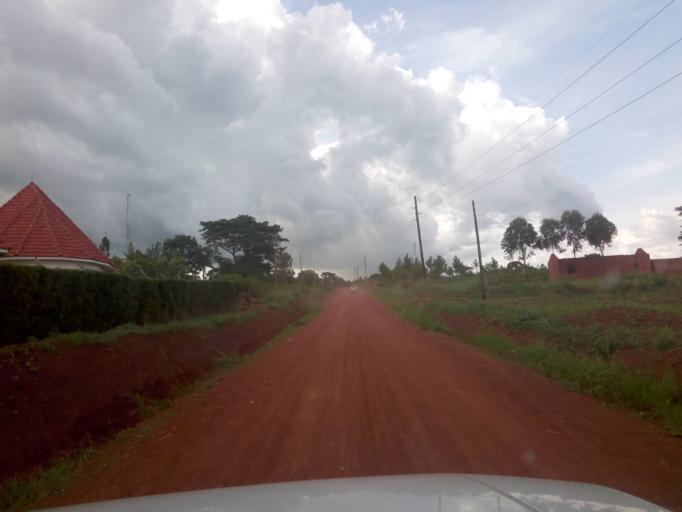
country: UG
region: Western Region
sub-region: Masindi District
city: Masindi
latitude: 1.6854
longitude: 31.7240
